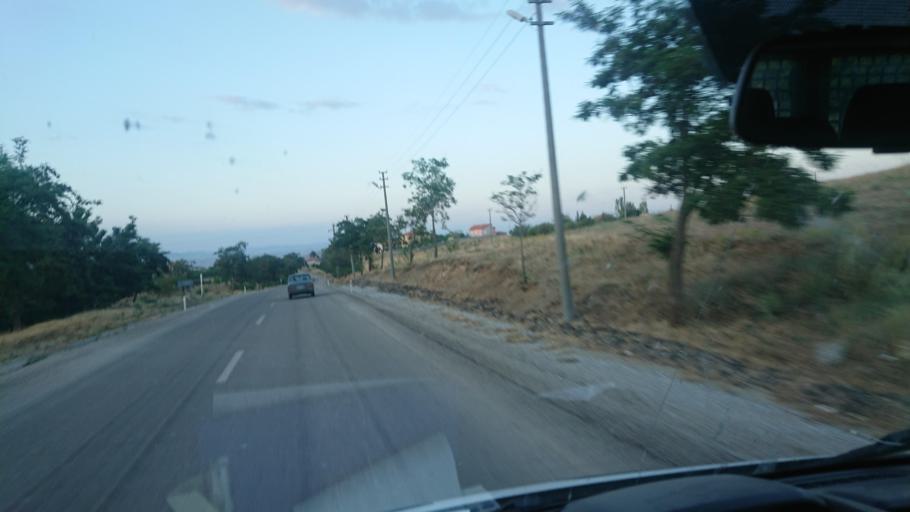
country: TR
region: Aksaray
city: Sariyahsi
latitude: 38.9744
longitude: 33.8331
